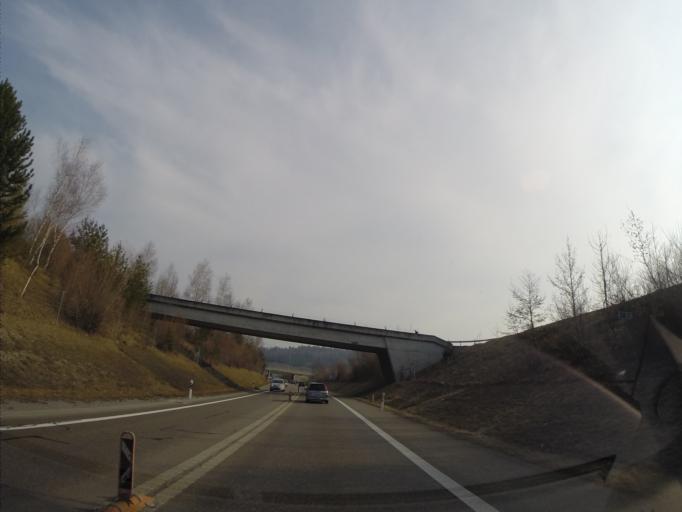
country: CH
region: Zurich
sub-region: Bezirk Winterthur
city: Wuelflingen (Kreis 6) / Lindenplatz
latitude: 47.5293
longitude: 8.6958
